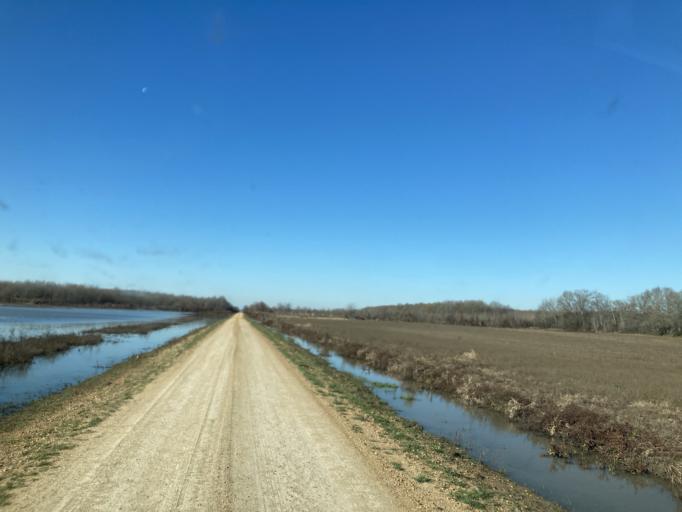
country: US
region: Mississippi
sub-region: Yazoo County
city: Yazoo City
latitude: 32.9518
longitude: -90.6189
